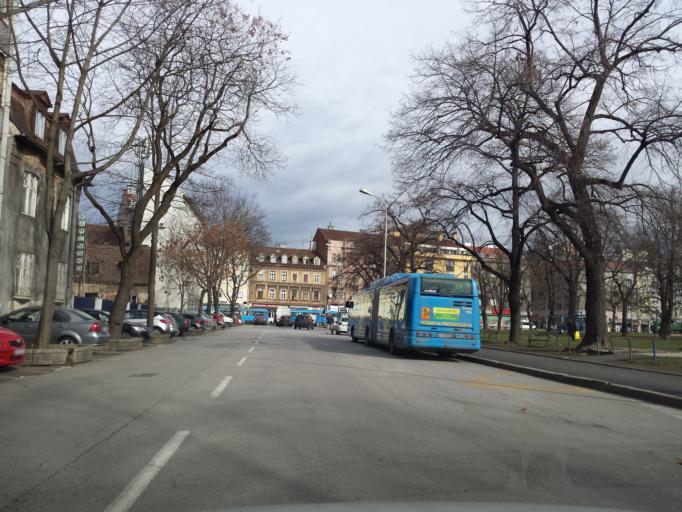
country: HR
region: Grad Zagreb
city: Zagreb - Centar
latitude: 45.8119
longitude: 15.9549
